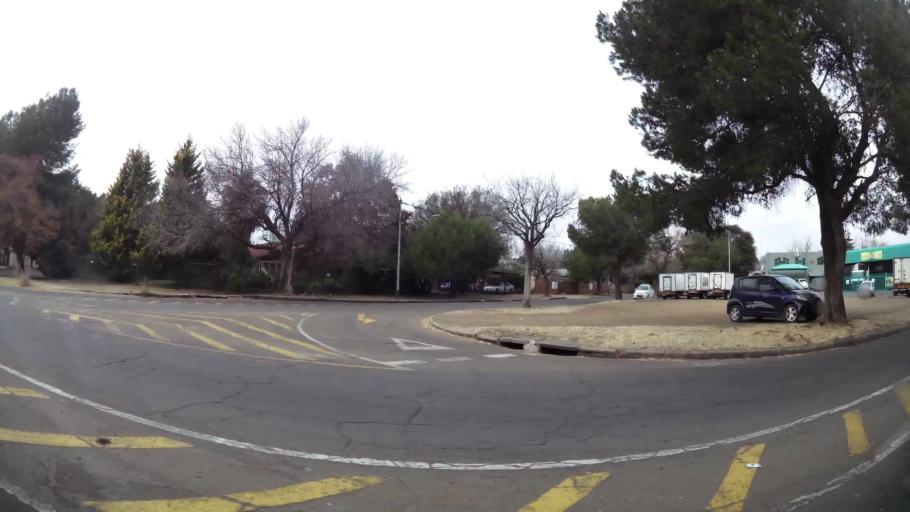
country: ZA
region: Orange Free State
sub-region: Mangaung Metropolitan Municipality
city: Bloemfontein
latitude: -29.1209
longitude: 26.1966
